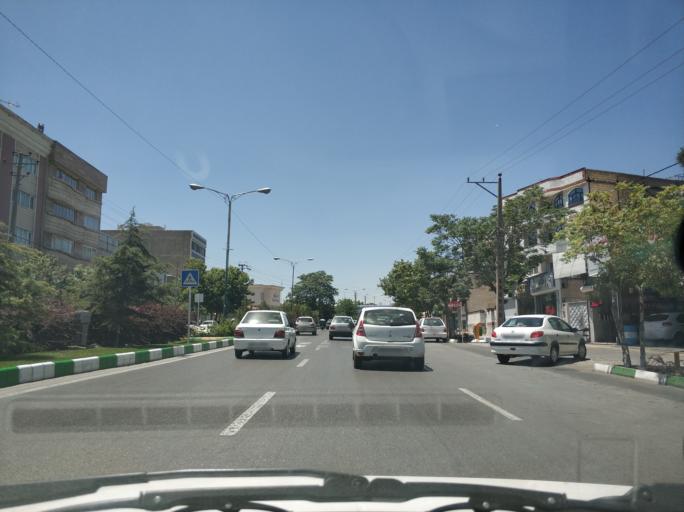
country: IR
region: Razavi Khorasan
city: Mashhad
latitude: 36.3127
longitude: 59.4929
